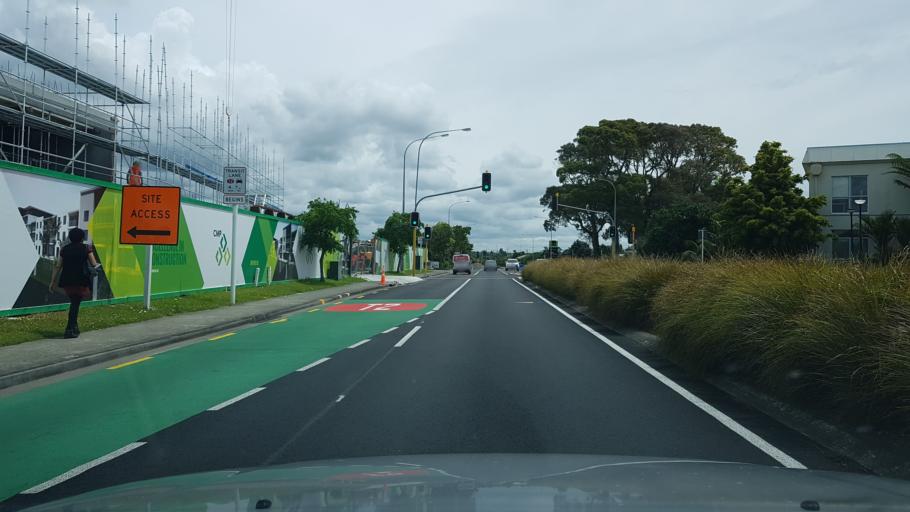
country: NZ
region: Auckland
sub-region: Auckland
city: North Shore
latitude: -36.7988
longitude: 174.7568
